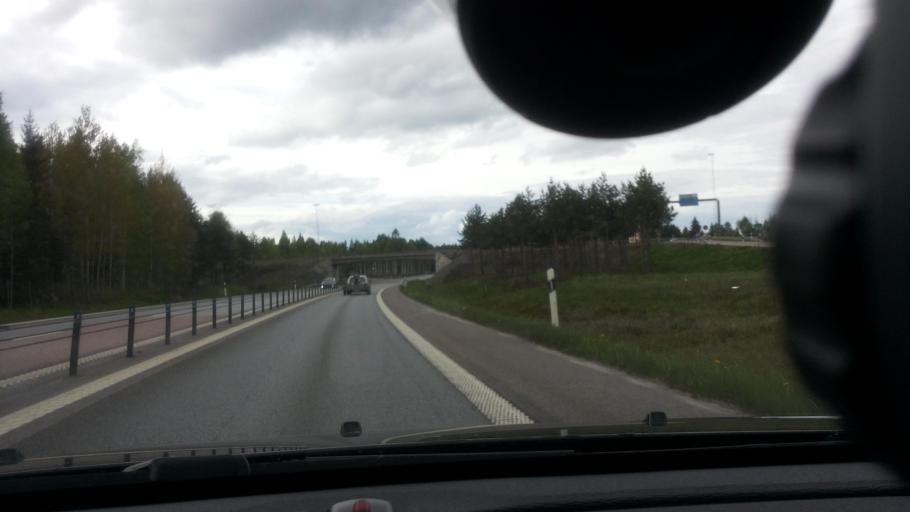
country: SE
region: Gaevleborg
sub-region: Gavle Kommun
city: Norrsundet
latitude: 60.9002
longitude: 17.0199
